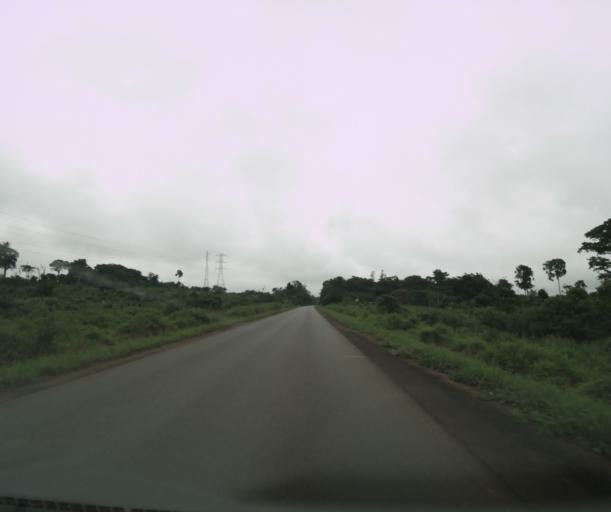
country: CM
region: Littoral
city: Edea
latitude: 3.6773
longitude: 10.1094
